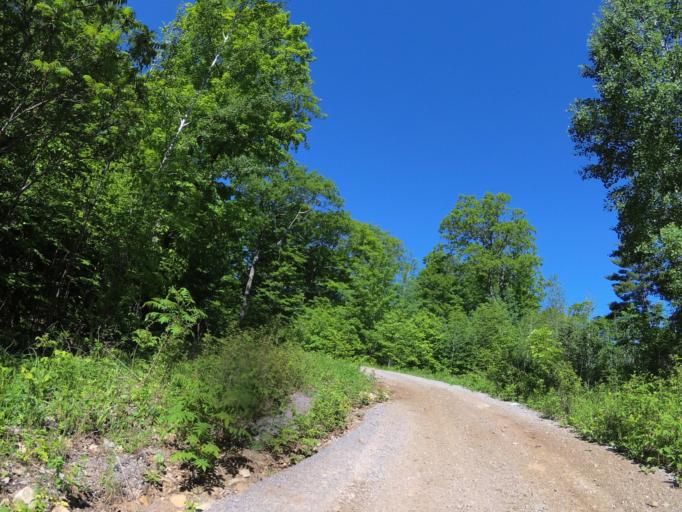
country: CA
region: Ontario
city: Renfrew
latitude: 45.0991
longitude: -77.0615
